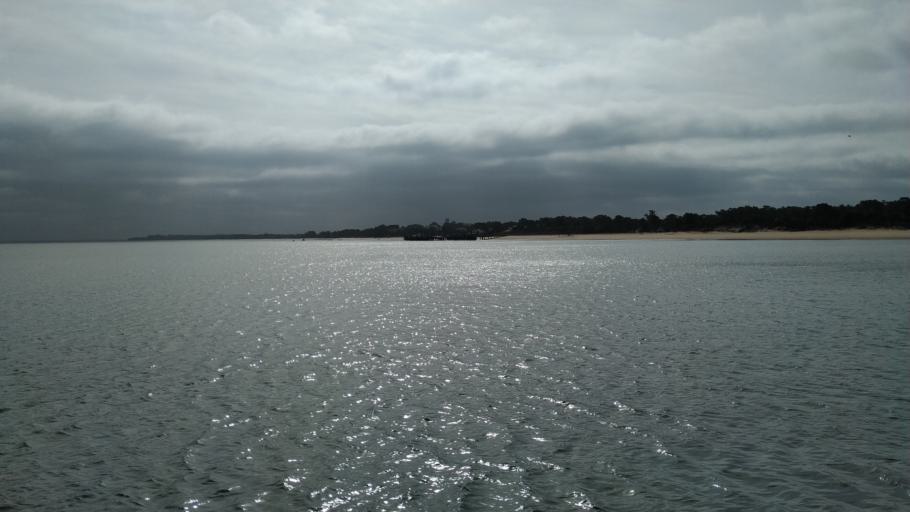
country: PT
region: Setubal
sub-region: Setubal
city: Setubal
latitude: 38.4731
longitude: -8.8662
